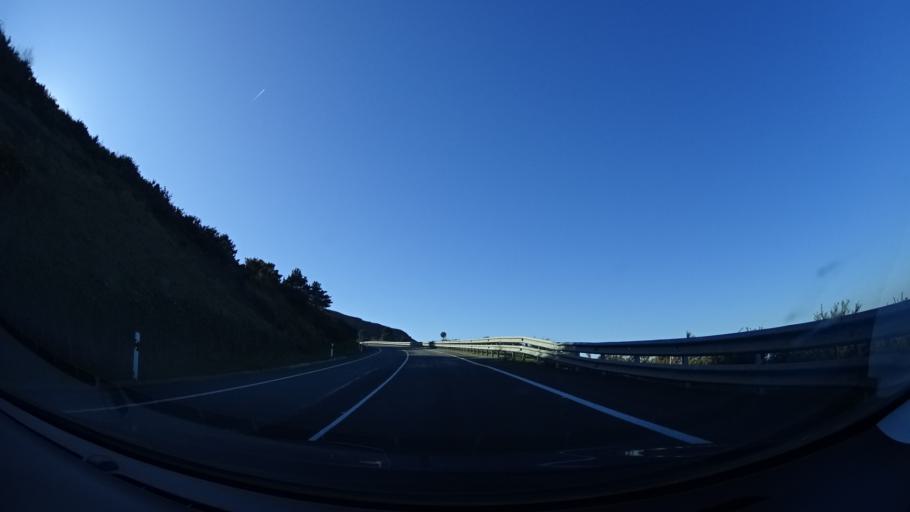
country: ES
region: Basque Country
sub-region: Bizkaia
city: Bakio
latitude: 43.4437
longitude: -2.7649
